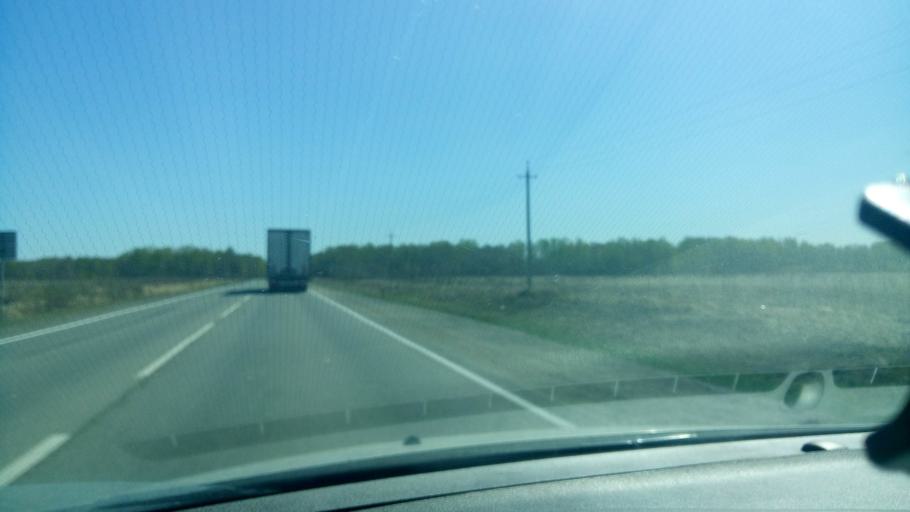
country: RU
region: Sverdlovsk
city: Bogdanovich
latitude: 56.7535
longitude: 62.1512
